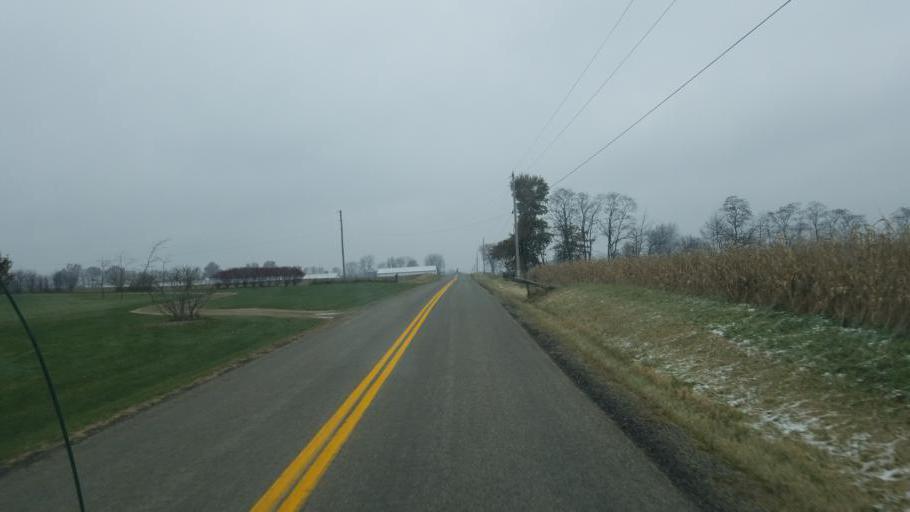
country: US
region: Ohio
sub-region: Huron County
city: New London
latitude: 41.0012
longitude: -82.3547
